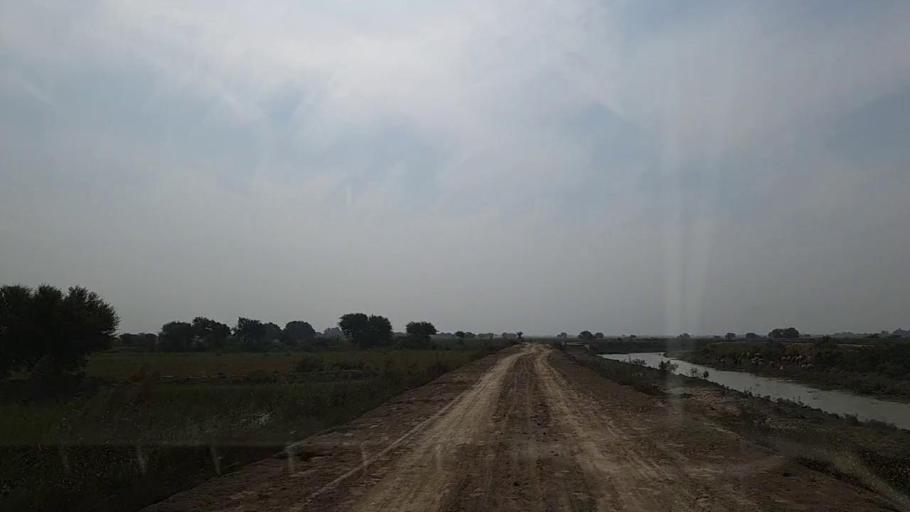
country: PK
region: Sindh
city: Mirpur Batoro
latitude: 24.6633
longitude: 68.2506
